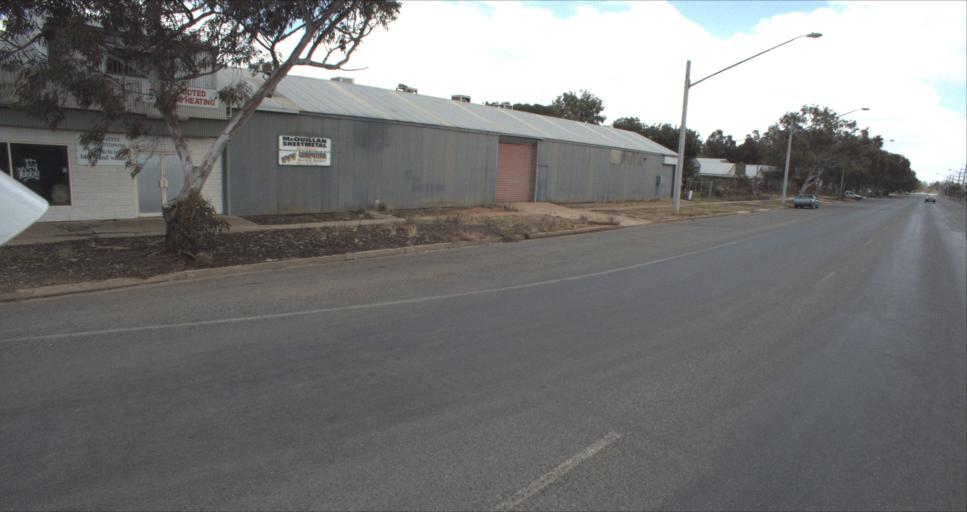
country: AU
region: New South Wales
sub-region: Leeton
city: Leeton
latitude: -34.5540
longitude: 146.3948
